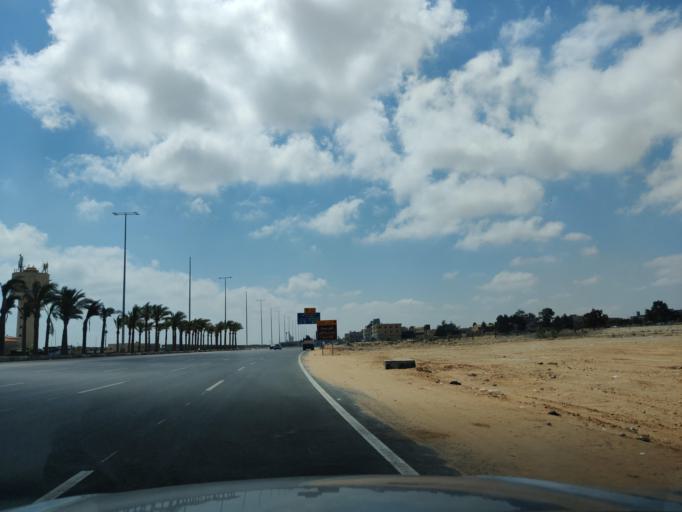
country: EG
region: Muhafazat Matruh
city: Al `Alamayn
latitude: 30.8441
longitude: 28.9442
